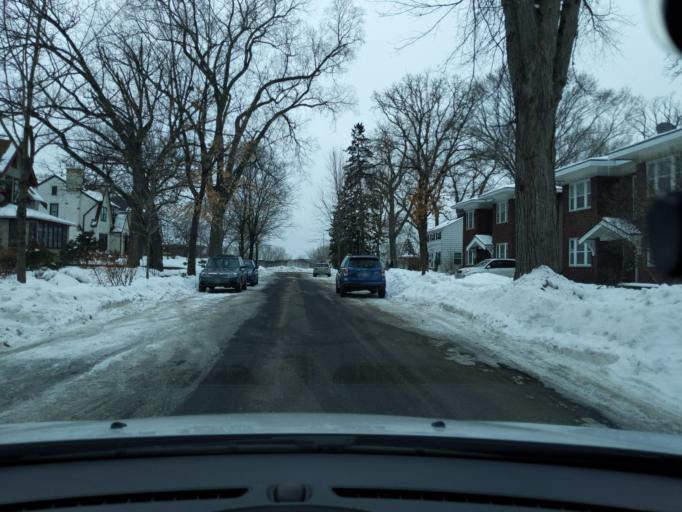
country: US
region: Minnesota
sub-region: Ramsey County
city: Lauderdale
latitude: 44.9614
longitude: -93.2090
